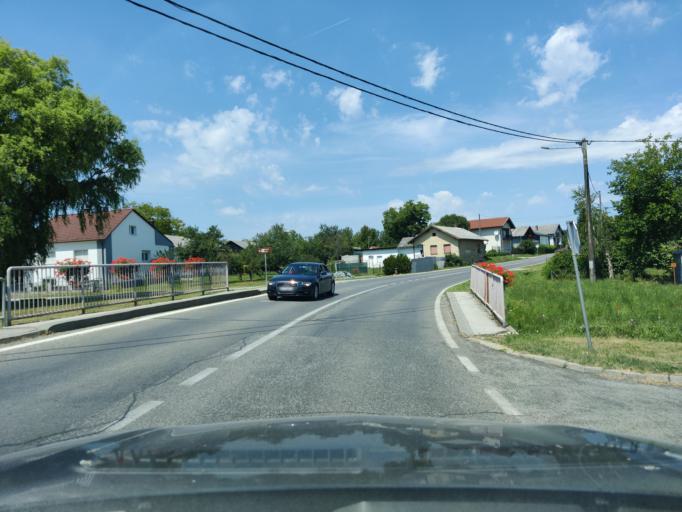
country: HR
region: Medimurska
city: Vratisinec
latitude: 46.4724
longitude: 16.4235
